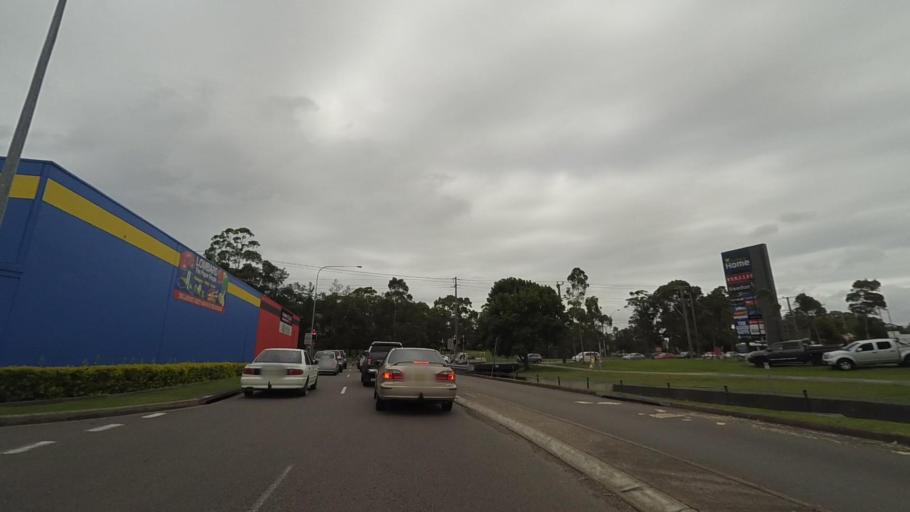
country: AU
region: New South Wales
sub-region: Lake Macquarie Shire
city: Highfields
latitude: -32.9401
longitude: 151.7075
